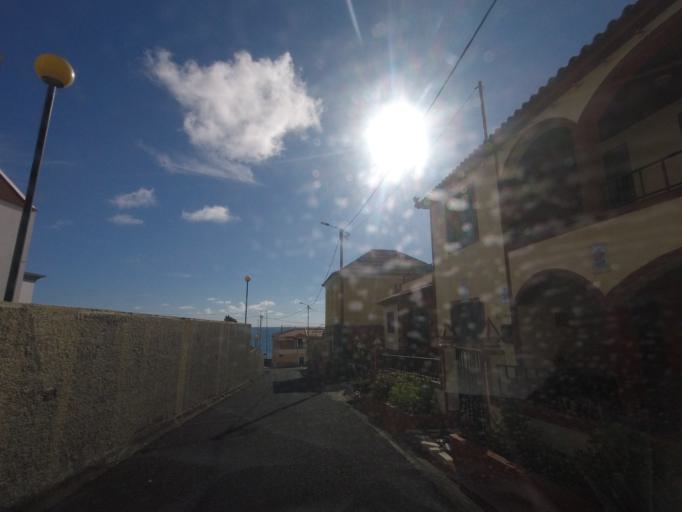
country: PT
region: Madeira
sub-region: Calheta
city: Faja da Ovelha
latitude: 32.7546
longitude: -17.2266
